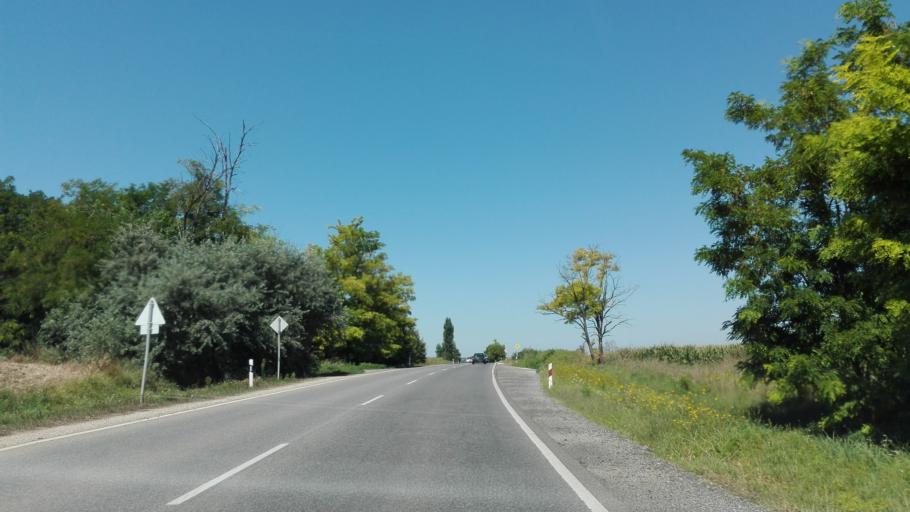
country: HU
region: Fejer
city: Mezoszilas
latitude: 46.8324
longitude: 18.4545
